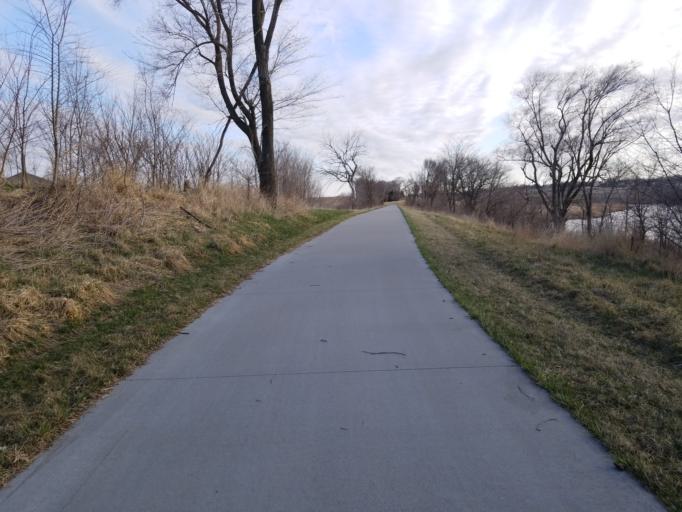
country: US
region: Nebraska
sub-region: Sarpy County
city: Chalco
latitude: 41.1531
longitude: -96.1133
